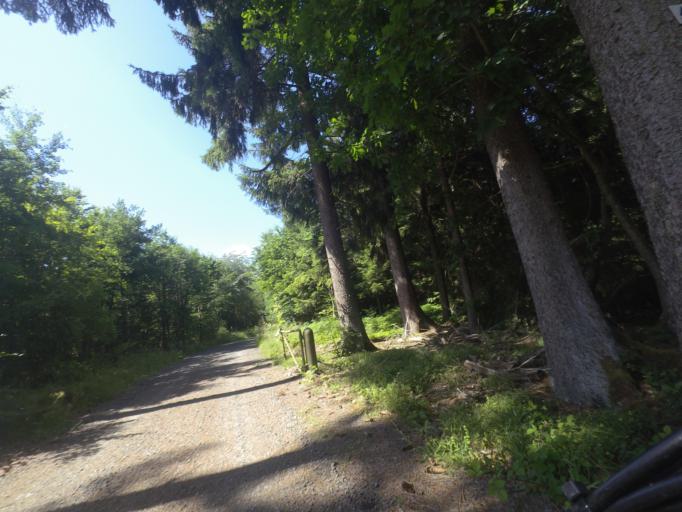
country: DE
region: Rheinland-Pfalz
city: Junkerath
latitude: 50.3246
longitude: 6.5595
